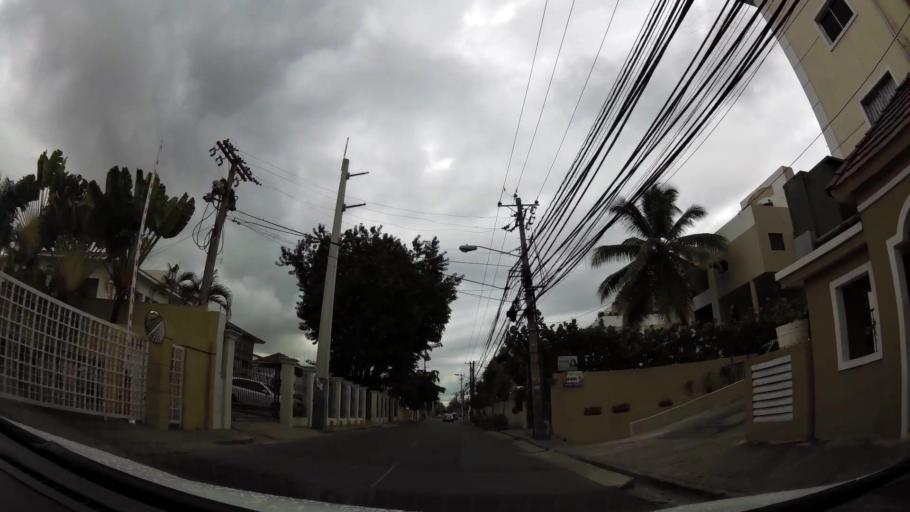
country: DO
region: Nacional
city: La Agustina
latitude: 18.4870
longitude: -69.9372
